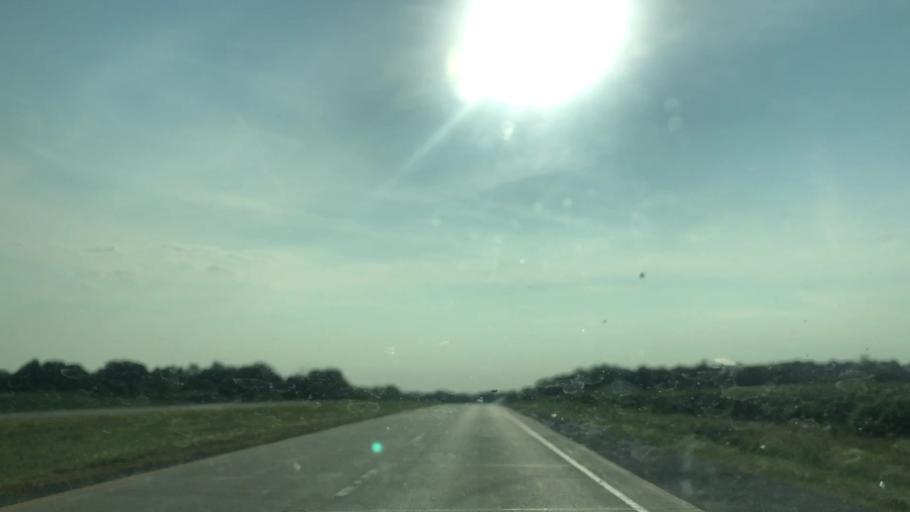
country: US
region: Iowa
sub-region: Story County
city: Nevada
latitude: 42.0080
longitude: -93.3667
